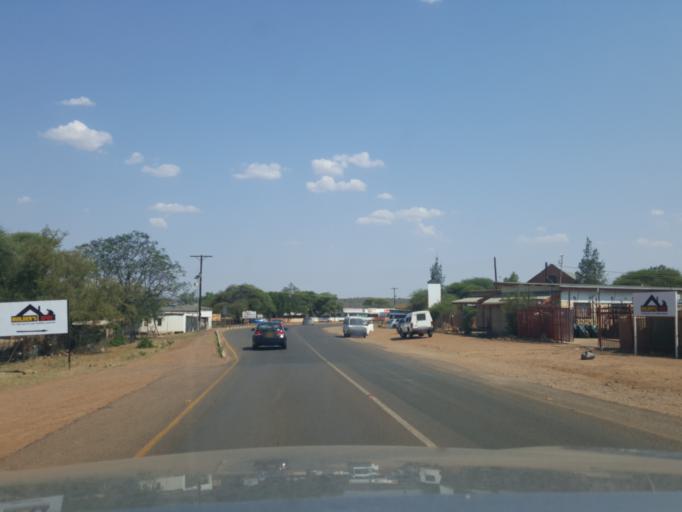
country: BW
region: South East
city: Ramotswa
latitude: -24.8475
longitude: 25.8298
